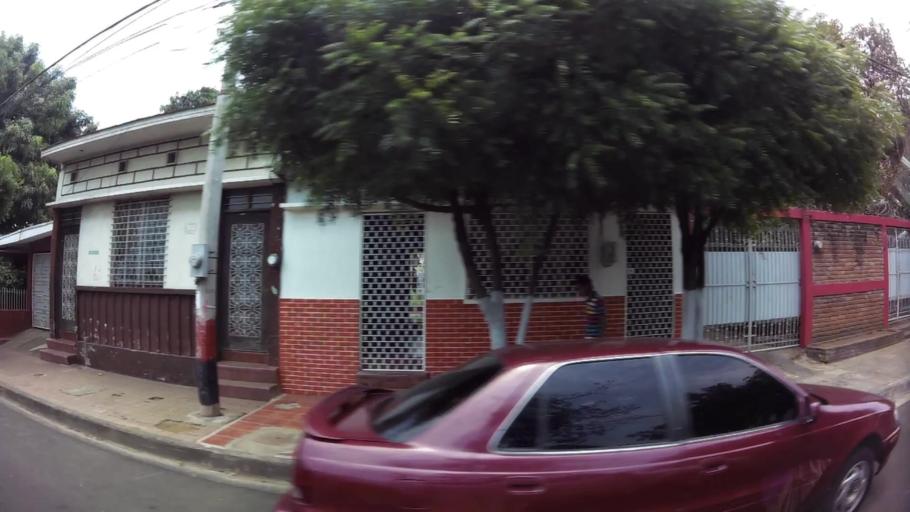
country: NI
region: Managua
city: Managua
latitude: 12.1338
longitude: -86.2946
